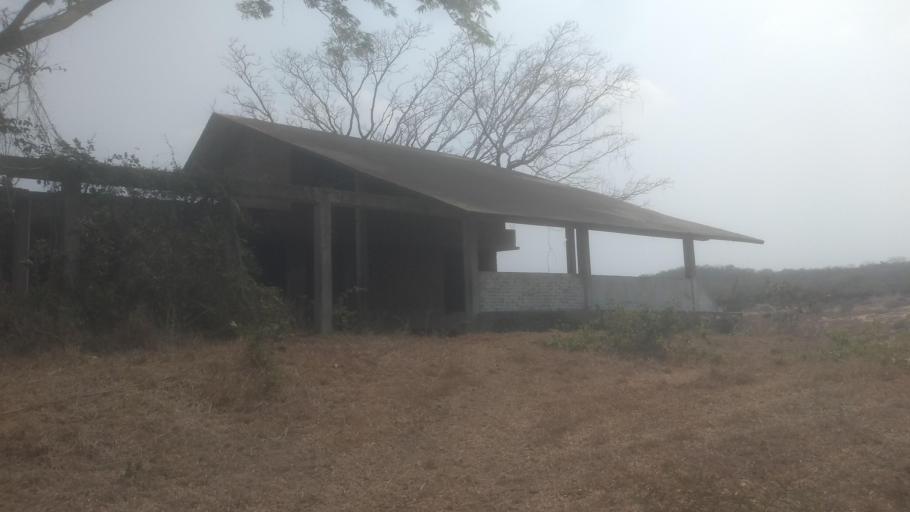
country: MX
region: Veracruz
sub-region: Veracruz
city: Fraccionamiento Geovillas los Pinos
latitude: 19.2355
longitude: -96.2398
